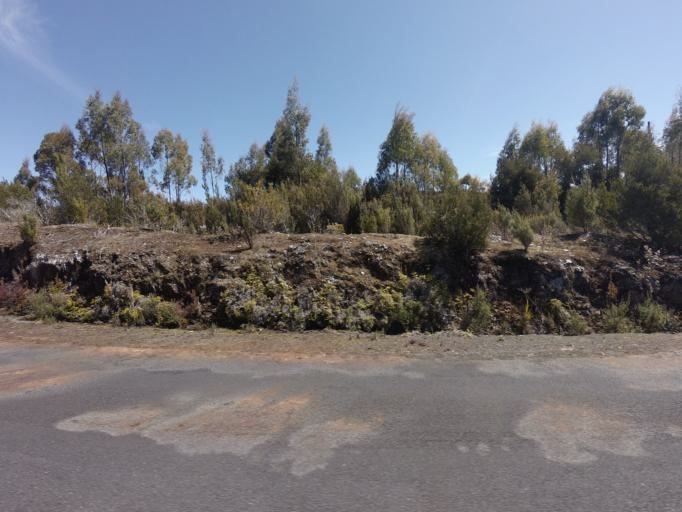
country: AU
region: Tasmania
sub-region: Huon Valley
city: Geeveston
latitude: -42.8068
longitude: 146.0974
